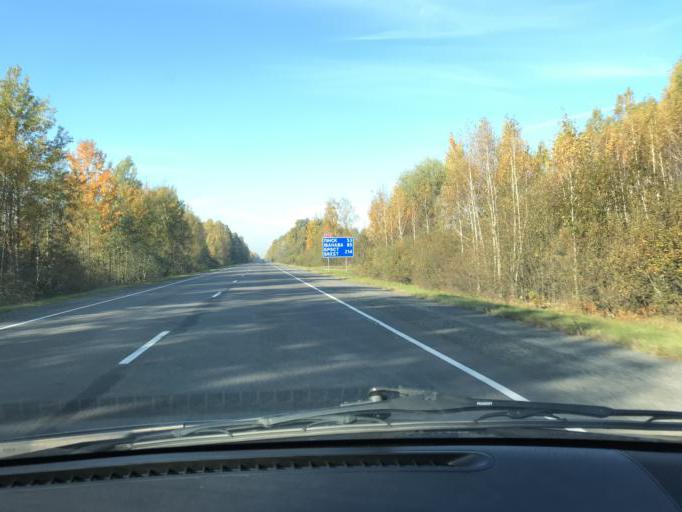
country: BY
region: Brest
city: Horad Luninyets
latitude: 52.2998
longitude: 26.7263
